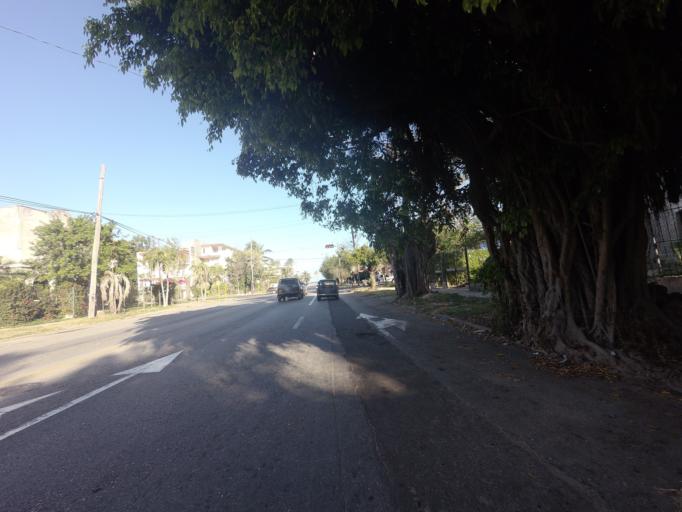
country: CU
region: La Habana
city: Havana
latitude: 23.1208
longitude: -82.4258
